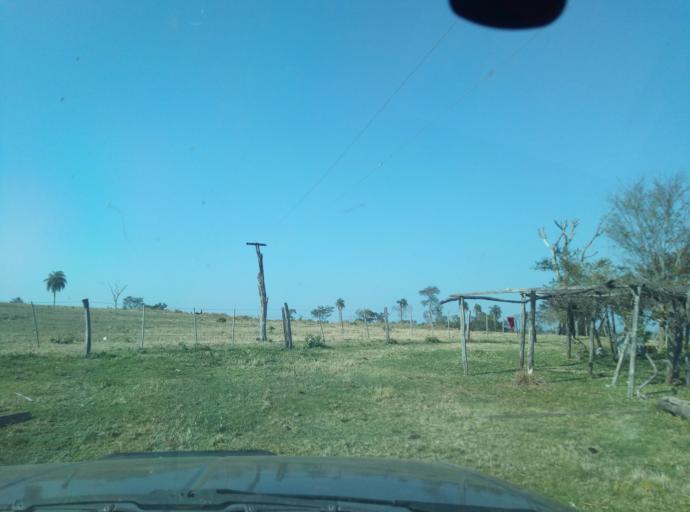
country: PY
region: Caaguazu
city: San Joaquin
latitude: -25.1769
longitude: -56.1134
